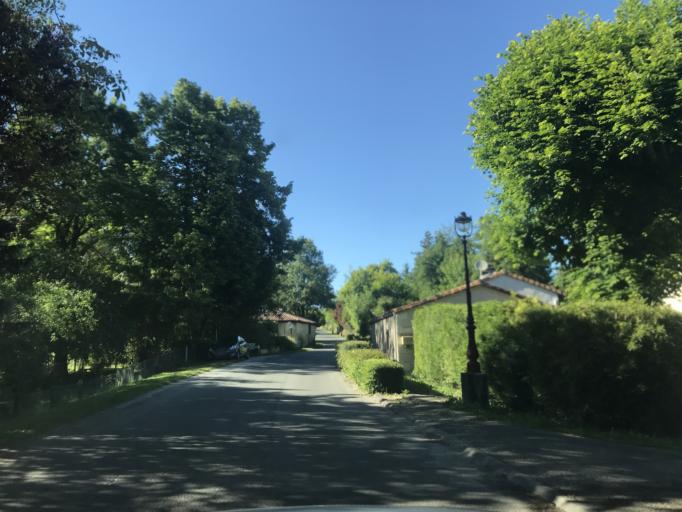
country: FR
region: Poitou-Charentes
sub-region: Departement de la Charente
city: Chalais
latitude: 45.2508
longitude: 0.0032
